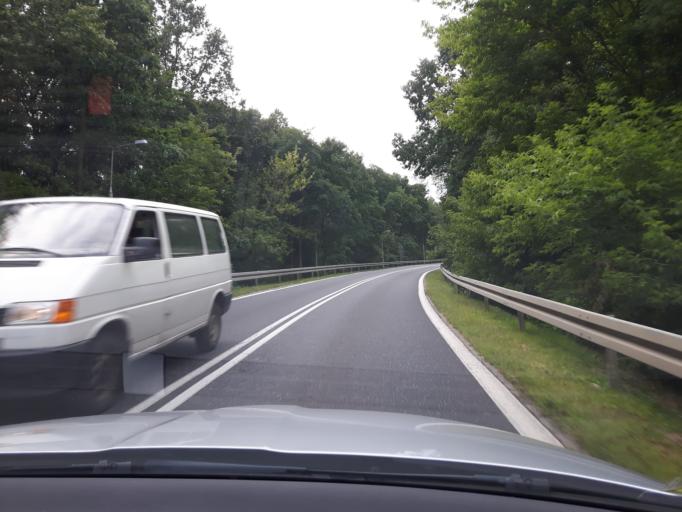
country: PL
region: Masovian Voivodeship
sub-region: Powiat legionowski
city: Wieliszew
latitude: 52.4438
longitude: 20.9949
